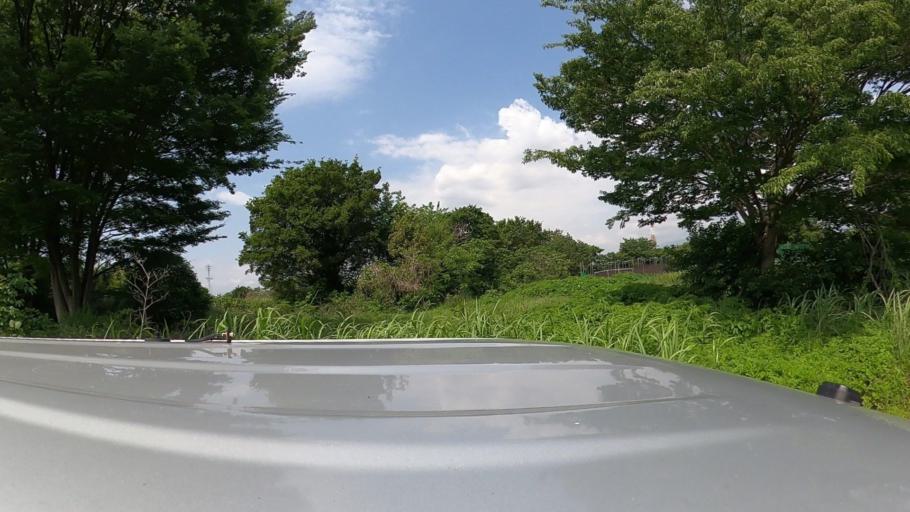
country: JP
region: Kanagawa
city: Chigasaki
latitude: 35.3501
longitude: 139.3732
